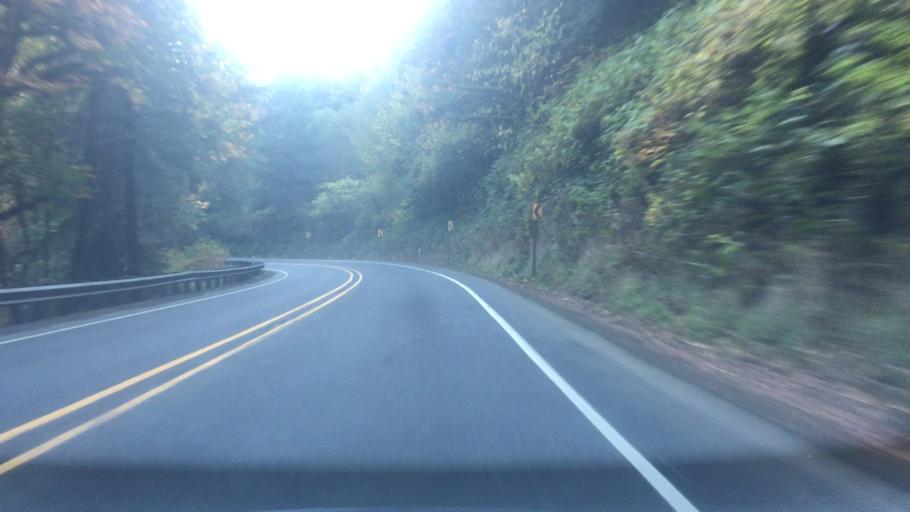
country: US
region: Oregon
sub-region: Lincoln County
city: Rose Lodge
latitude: 45.0073
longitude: -123.9188
